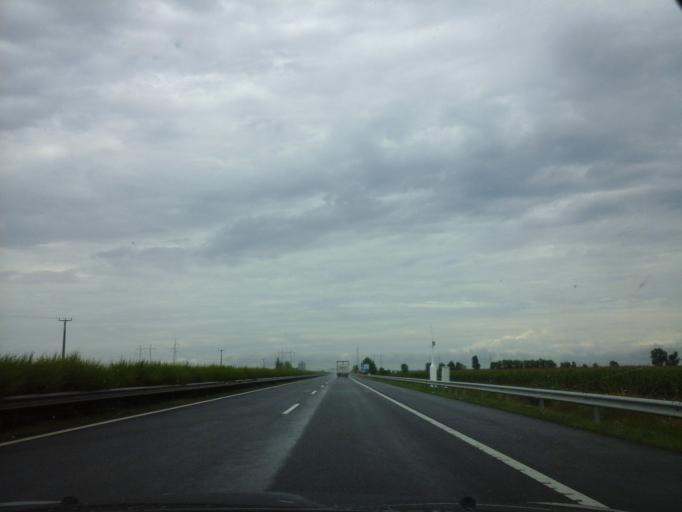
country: HU
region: Hajdu-Bihar
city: Gorbehaza
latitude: 47.7986
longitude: 21.2233
